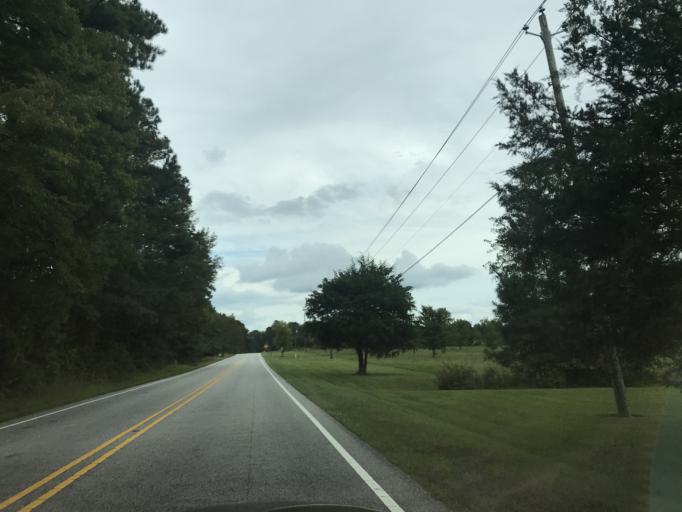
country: US
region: North Carolina
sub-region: Franklin County
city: Youngsville
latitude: 36.0043
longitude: -78.4325
